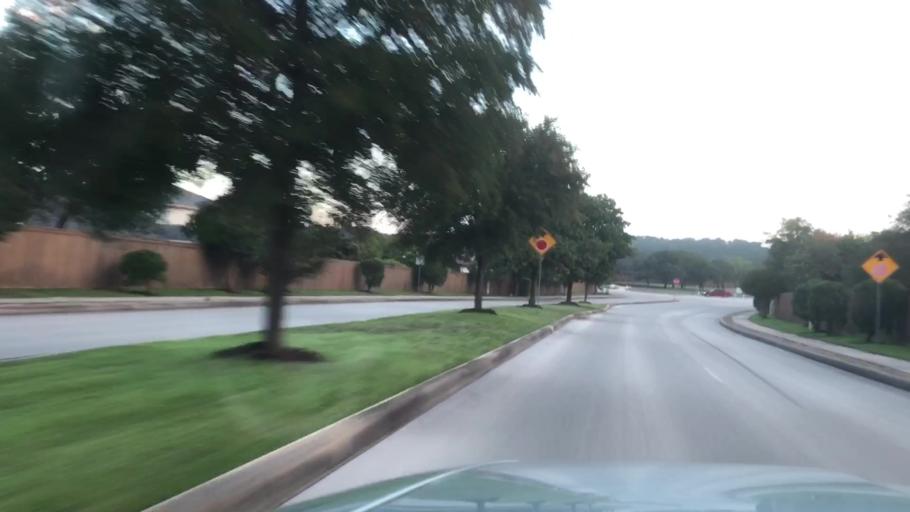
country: US
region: Texas
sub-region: Bexar County
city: Helotes
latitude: 29.5504
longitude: -98.6464
